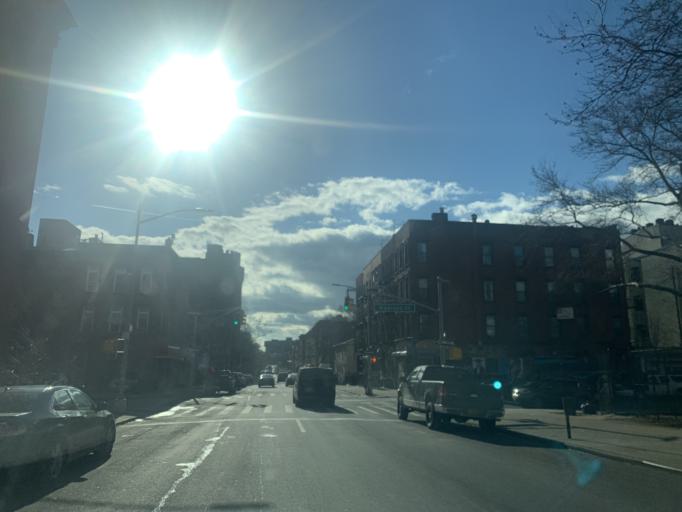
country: US
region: New York
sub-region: Kings County
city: Brooklyn
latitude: 40.6865
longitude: -73.9387
